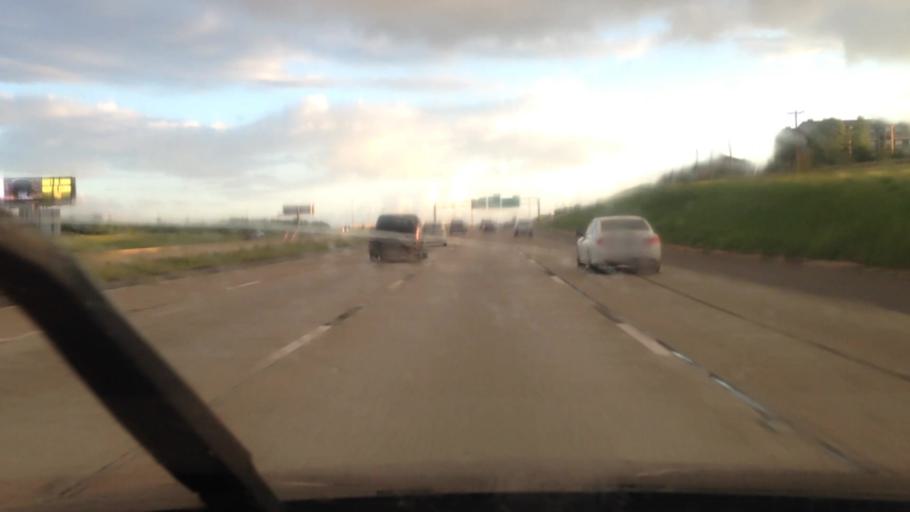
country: US
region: Texas
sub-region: Tarrant County
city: White Settlement
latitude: 32.7510
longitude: -97.4799
